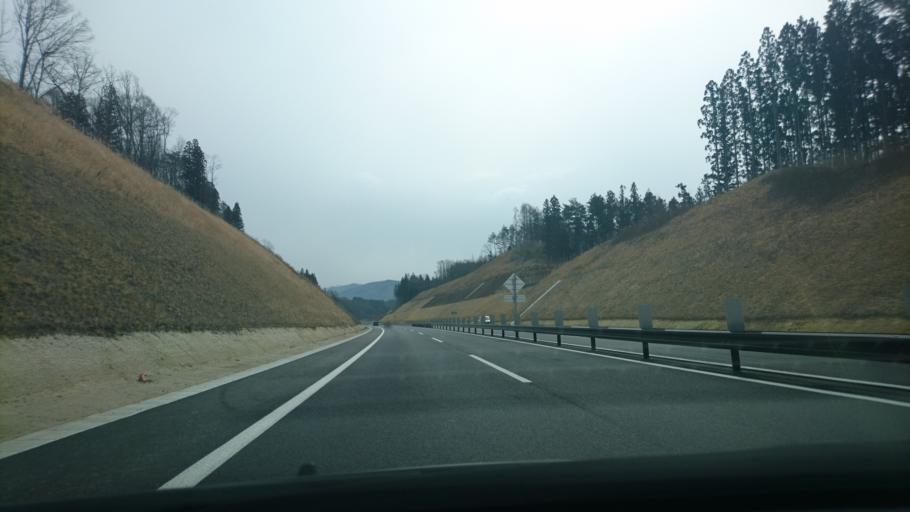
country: JP
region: Iwate
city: Tono
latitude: 39.2782
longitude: 141.5599
